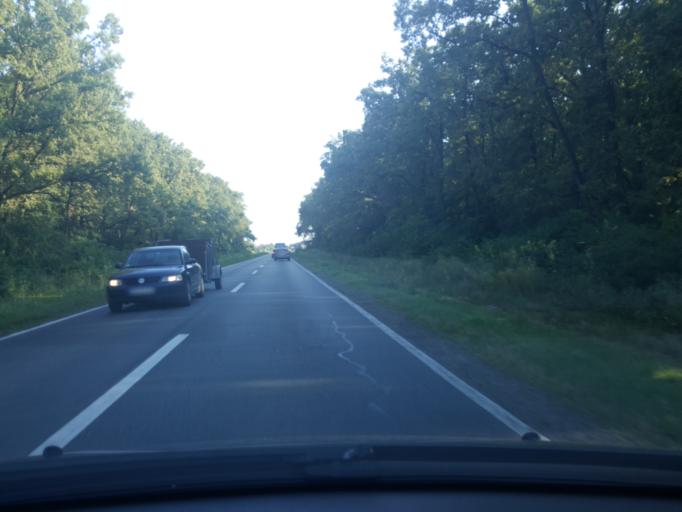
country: RS
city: Hrtkovci
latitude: 44.8965
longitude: 19.7642
